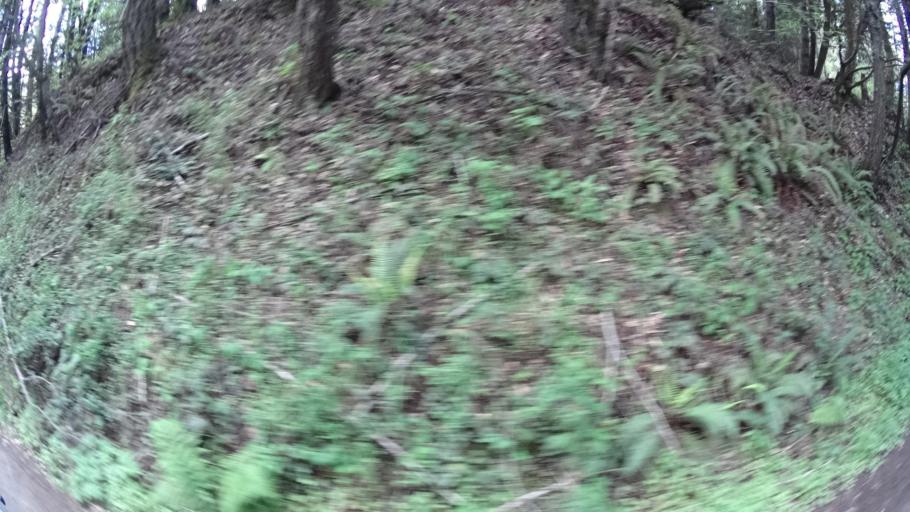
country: US
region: California
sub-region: Humboldt County
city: Blue Lake
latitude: 40.7844
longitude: -123.8795
